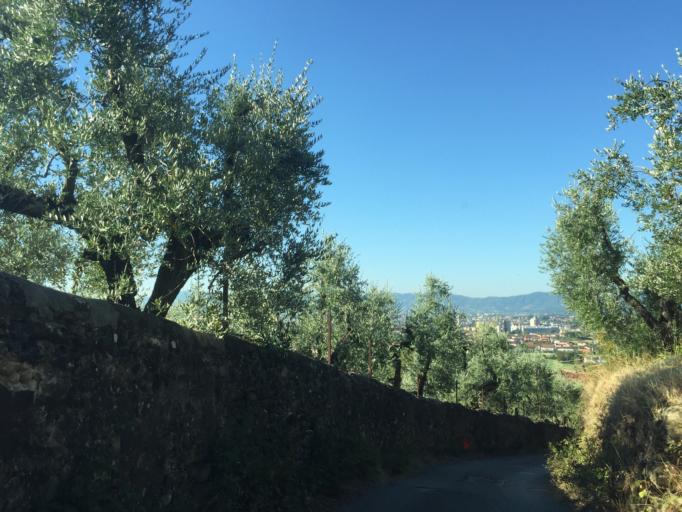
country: IT
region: Tuscany
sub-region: Provincia di Pistoia
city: Pistoia
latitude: 43.9571
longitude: 10.9411
